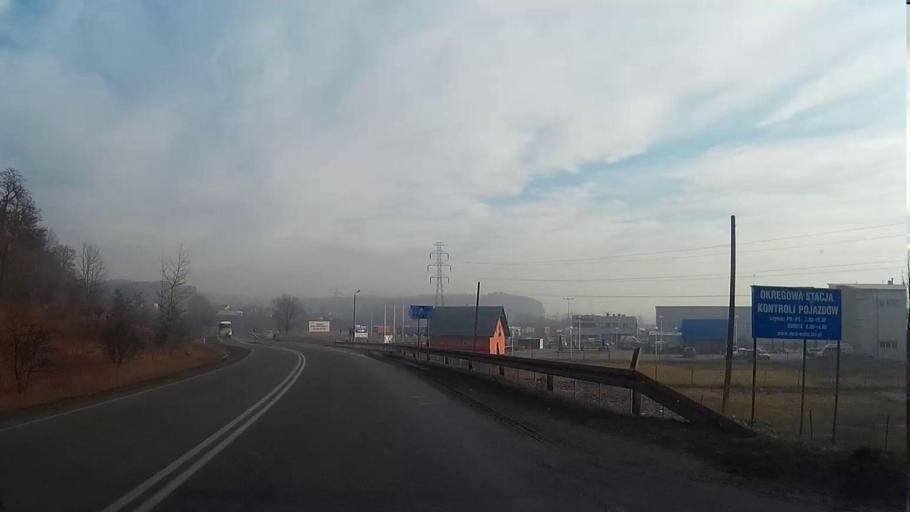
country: PL
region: Lesser Poland Voivodeship
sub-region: Powiat krakowski
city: Kryspinow
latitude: 50.0410
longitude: 19.8027
